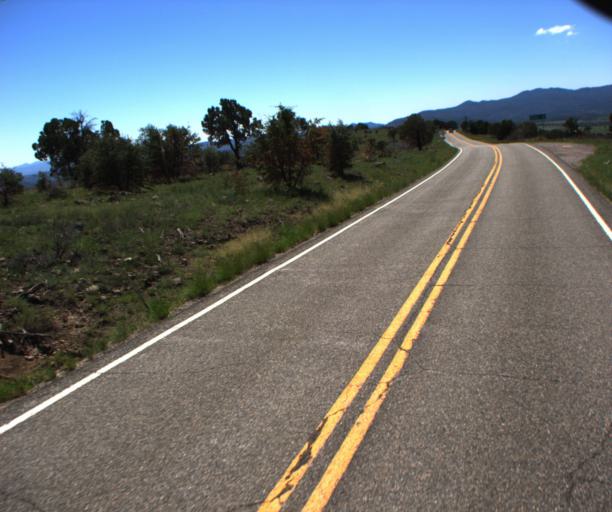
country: US
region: Arizona
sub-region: Greenlee County
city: Morenci
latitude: 33.3451
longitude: -109.3467
